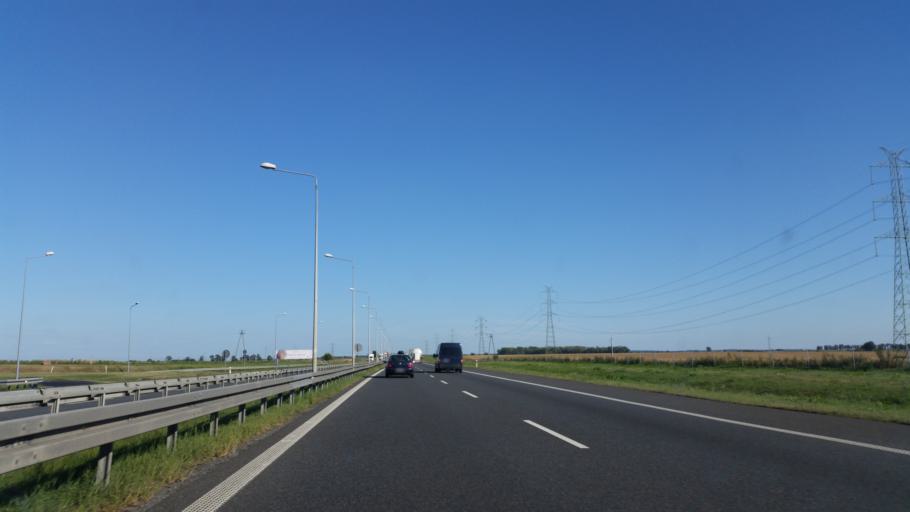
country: PL
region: Opole Voivodeship
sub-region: Powiat brzeski
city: Olszanka
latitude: 50.7554
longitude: 17.4329
